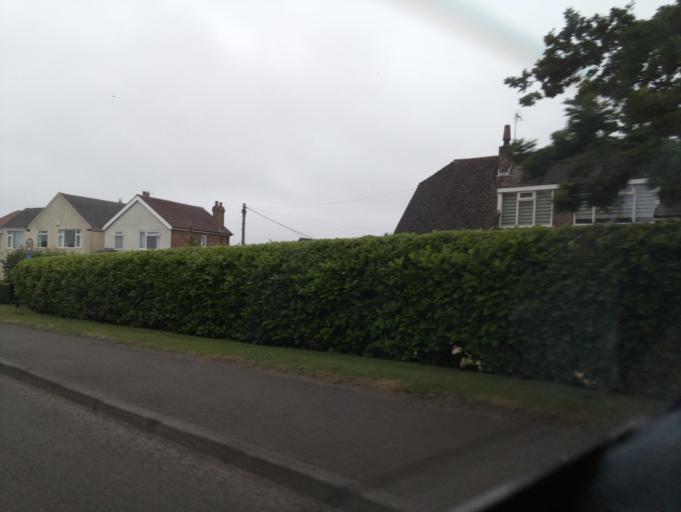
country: GB
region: England
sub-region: Derbyshire
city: Netherseal
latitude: 52.7417
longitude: -1.5716
